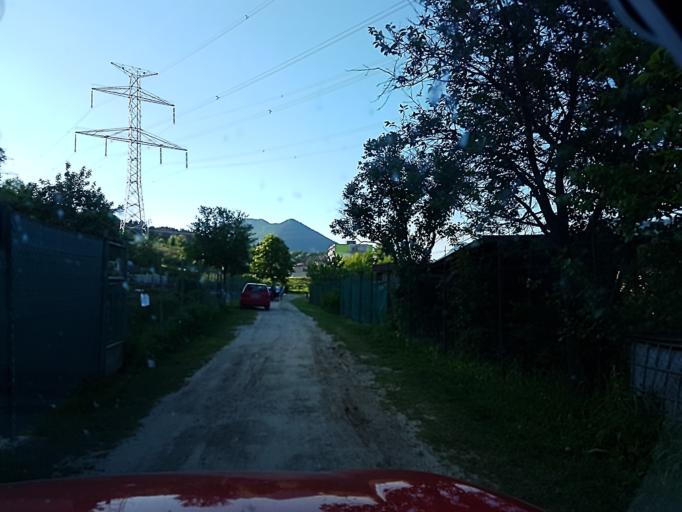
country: SK
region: Zilinsky
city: Ruzomberok
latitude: 49.0635
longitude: 19.2989
